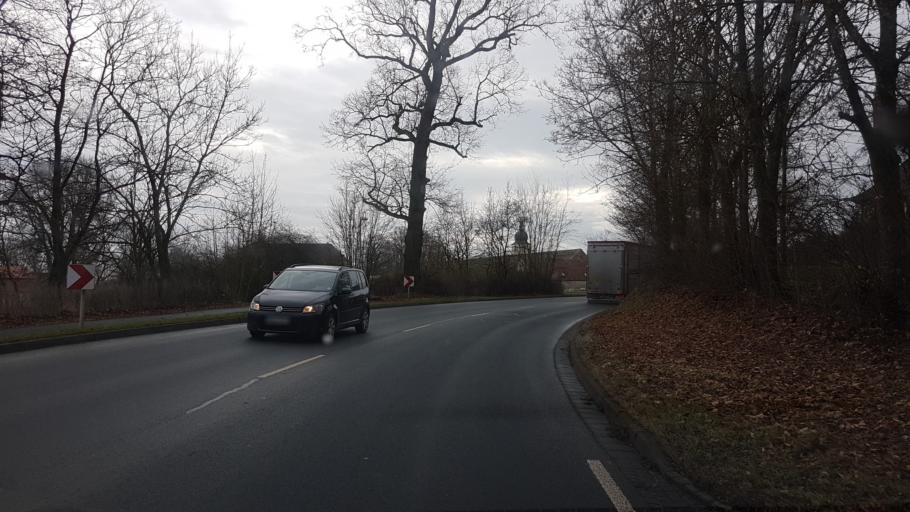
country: DE
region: Bavaria
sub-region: Regierungsbezirk Unterfranken
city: Rentweinsdorf
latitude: 50.0664
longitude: 10.7996
